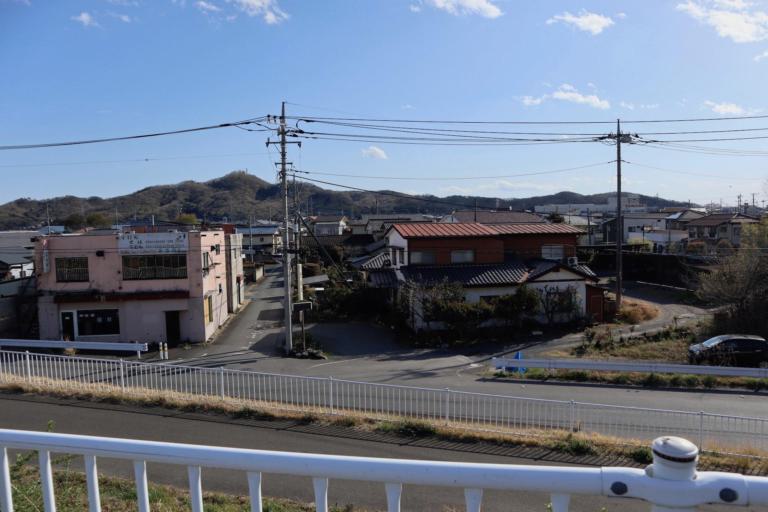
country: JP
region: Gunma
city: Kiryu
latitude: 36.3953
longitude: 139.3310
